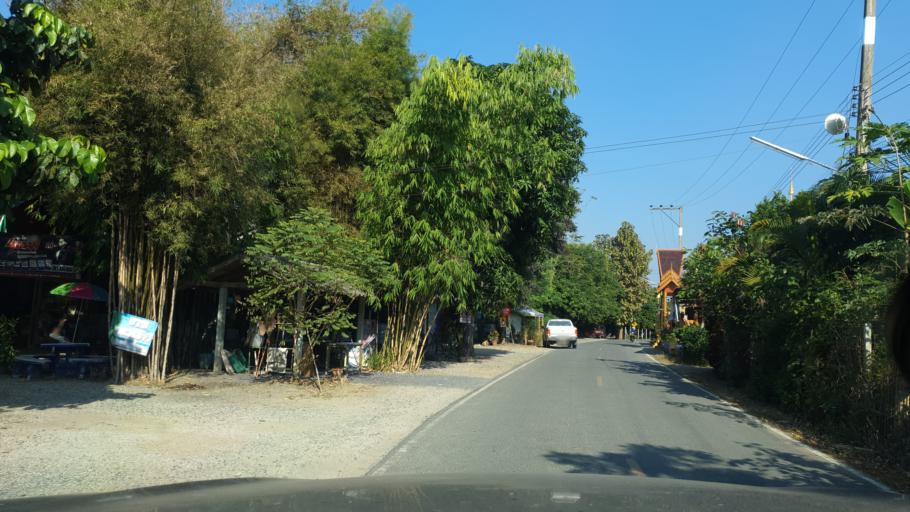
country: TH
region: Chiang Mai
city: Saraphi
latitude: 18.7024
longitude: 99.0765
